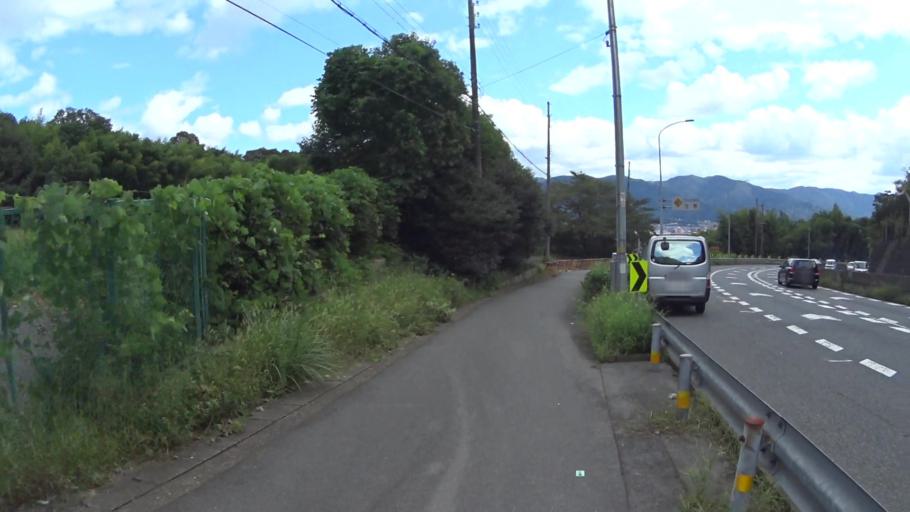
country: JP
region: Kyoto
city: Kyoto
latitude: 34.9888
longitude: 135.7945
